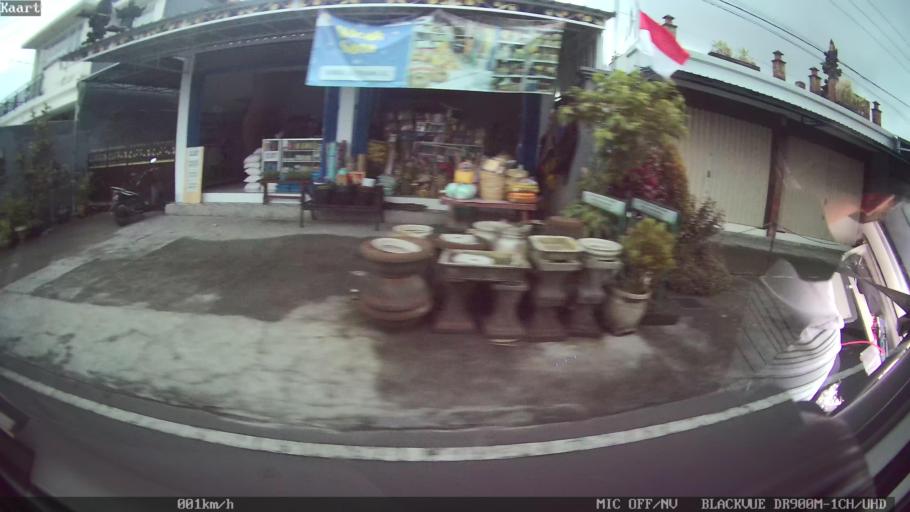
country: ID
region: Bali
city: Petang
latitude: -8.4054
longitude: 115.2192
